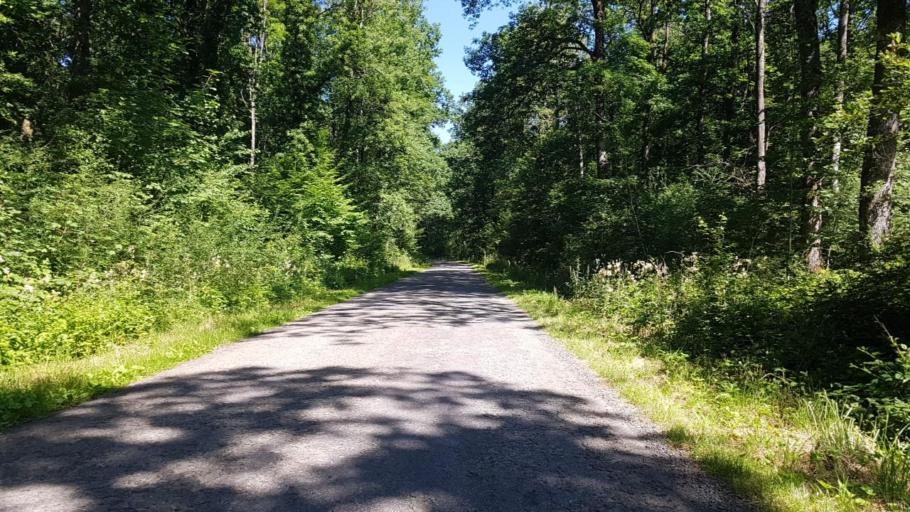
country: BE
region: Wallonia
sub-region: Province du Hainaut
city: Momignies
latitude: 50.0762
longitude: 4.2304
